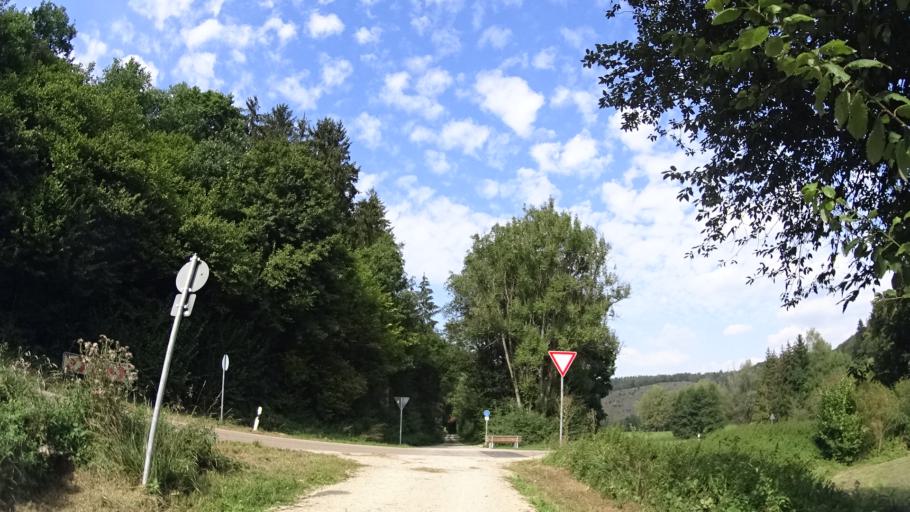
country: DE
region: Bavaria
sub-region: Lower Bavaria
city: Riedenburg
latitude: 48.9414
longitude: 11.6835
